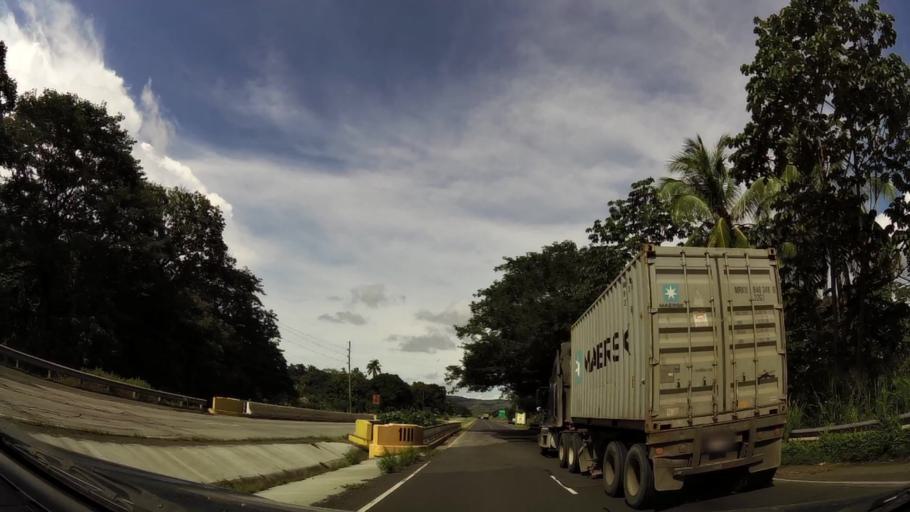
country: PA
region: Panama
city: Capira
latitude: 8.6884
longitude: -79.8690
